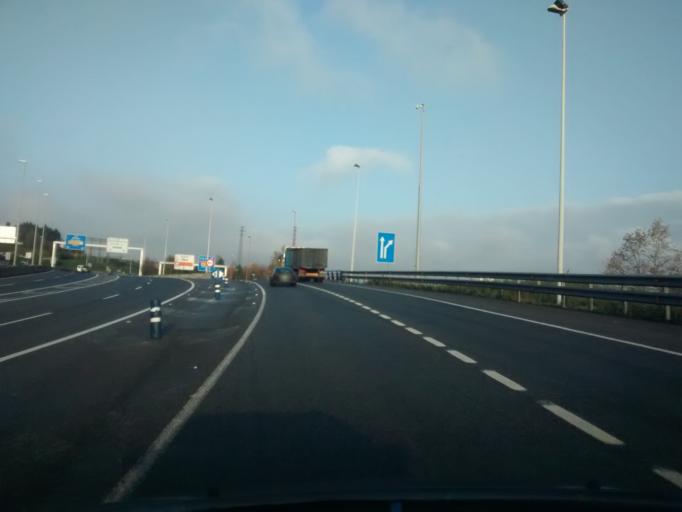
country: ES
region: Basque Country
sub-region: Bizkaia
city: Santutxu
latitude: 43.2427
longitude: -2.9281
